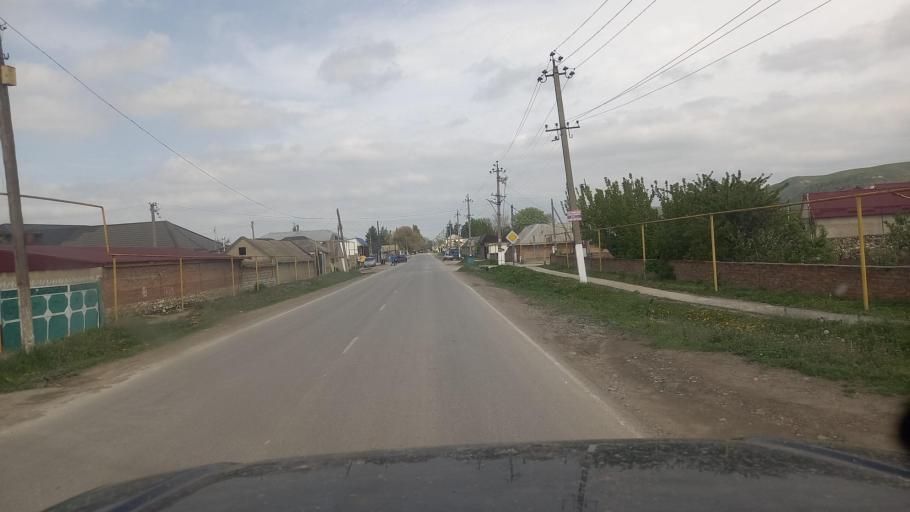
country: RU
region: Kabardino-Balkariya
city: Sarmakovo
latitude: 43.7401
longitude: 43.1879
